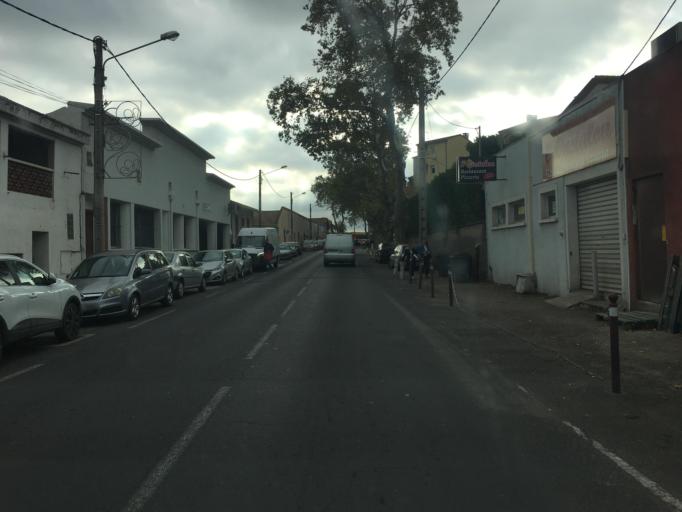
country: FR
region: Languedoc-Roussillon
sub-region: Departement de l'Herault
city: Nebian
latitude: 43.6249
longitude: 3.4341
